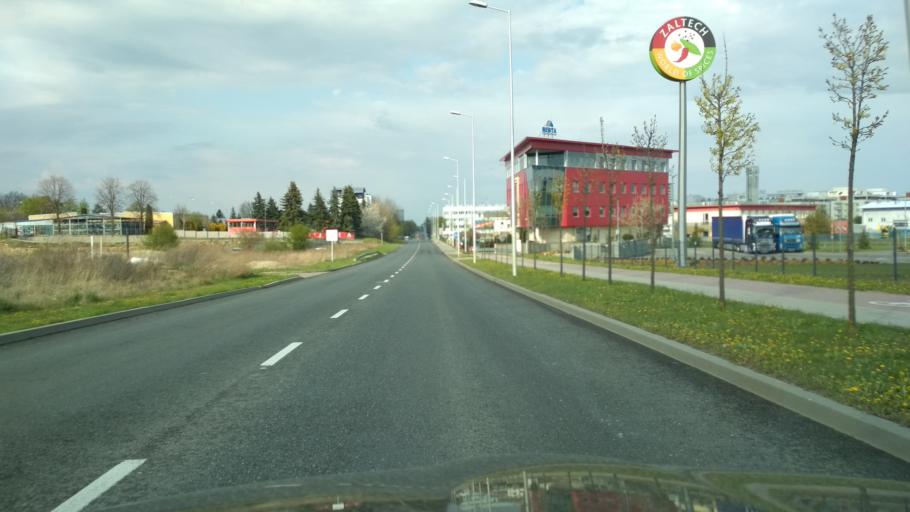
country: PL
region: Subcarpathian Voivodeship
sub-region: Powiat rzeszowski
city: Kielanowka
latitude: 50.0158
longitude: 21.9614
